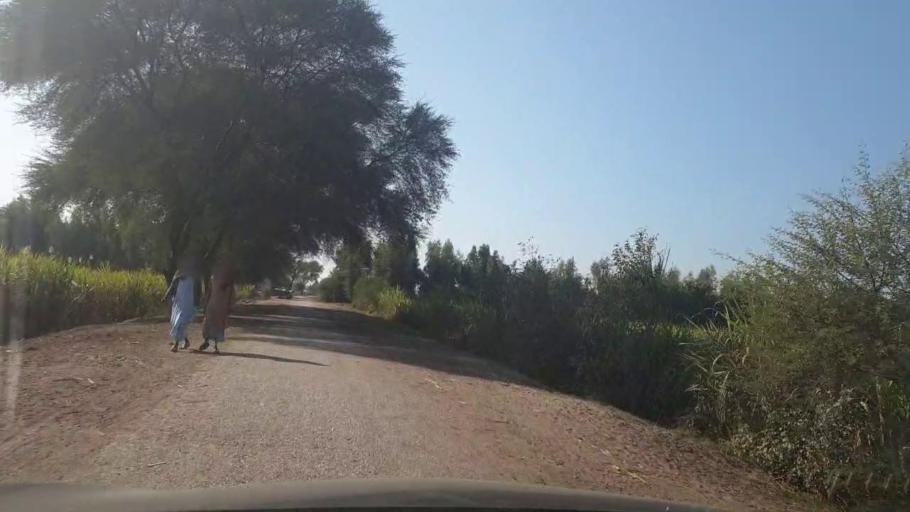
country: PK
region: Sindh
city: Mirpur Mathelo
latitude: 28.1447
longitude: 69.5956
